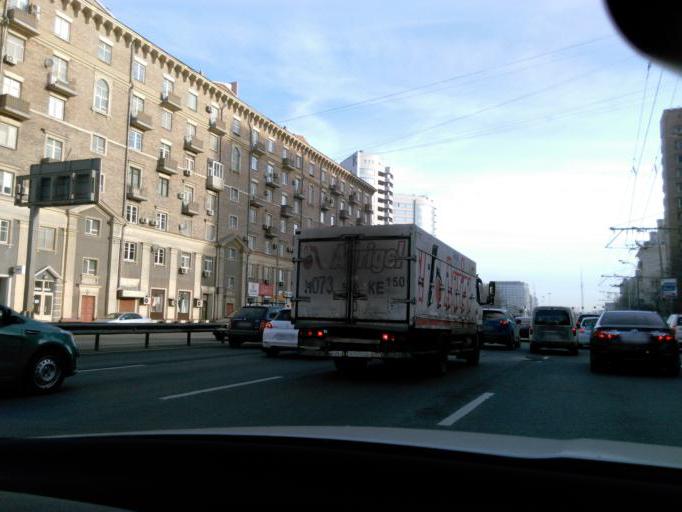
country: RU
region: Moskovskaya
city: Dorogomilovo
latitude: 55.7811
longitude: 37.5598
